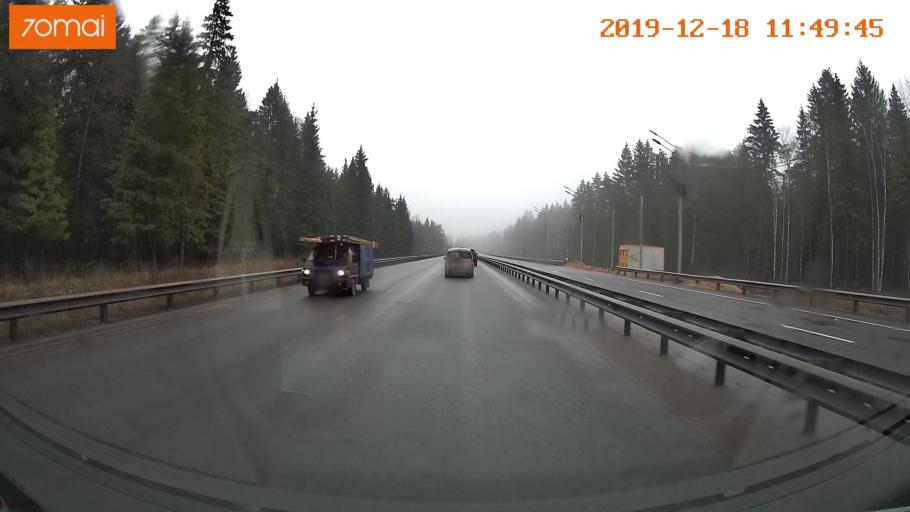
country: RU
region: Moskovskaya
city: Yershovo
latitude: 55.7801
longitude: 36.9138
